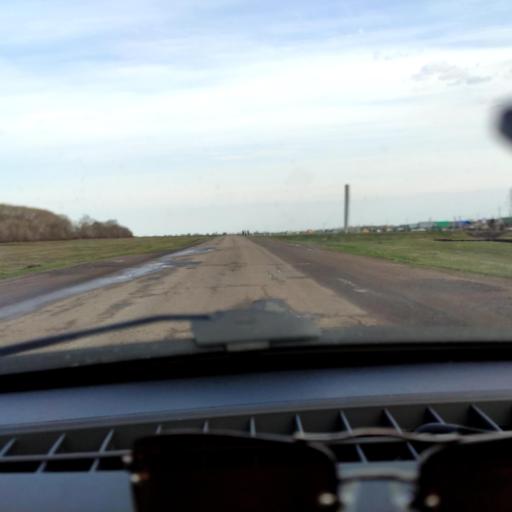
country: RU
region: Bashkortostan
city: Ulukulevo
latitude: 54.4661
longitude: 56.2298
